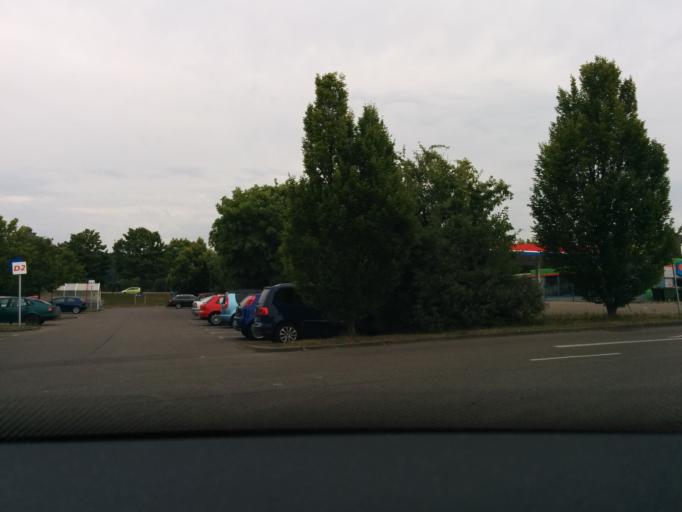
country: DE
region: Baden-Wuerttemberg
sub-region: Regierungsbezirk Stuttgart
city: Gerlingen
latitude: 48.8067
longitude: 9.0758
